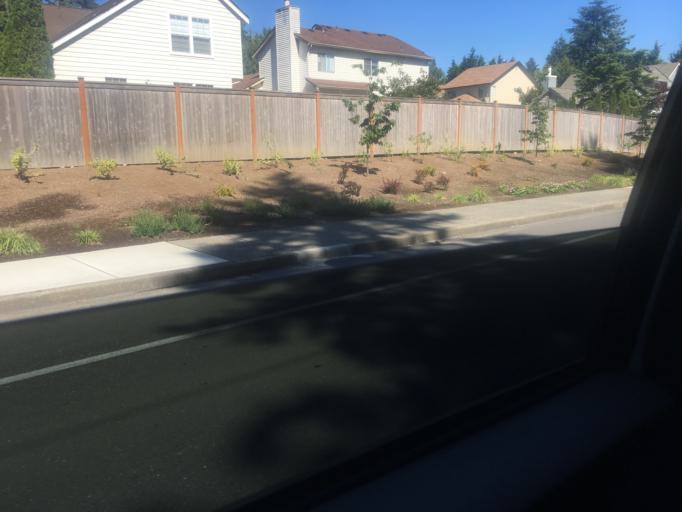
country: US
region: Washington
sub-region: King County
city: Bellevue
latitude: 47.6130
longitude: -122.1749
